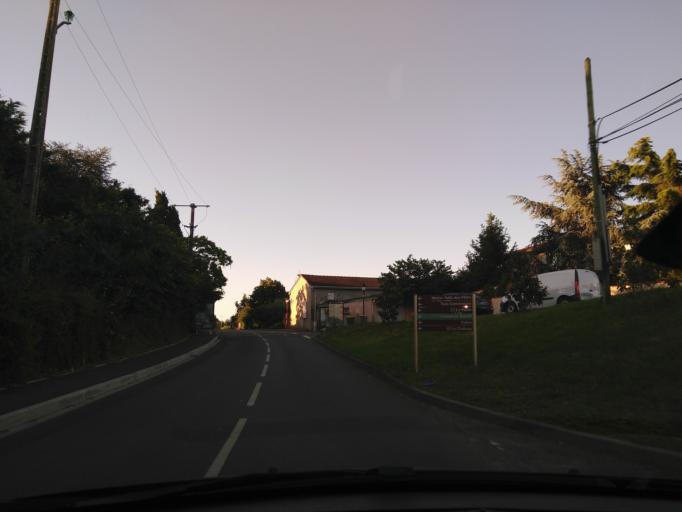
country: FR
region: Midi-Pyrenees
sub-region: Departement de la Haute-Garonne
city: Merville
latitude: 43.7248
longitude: 1.2975
